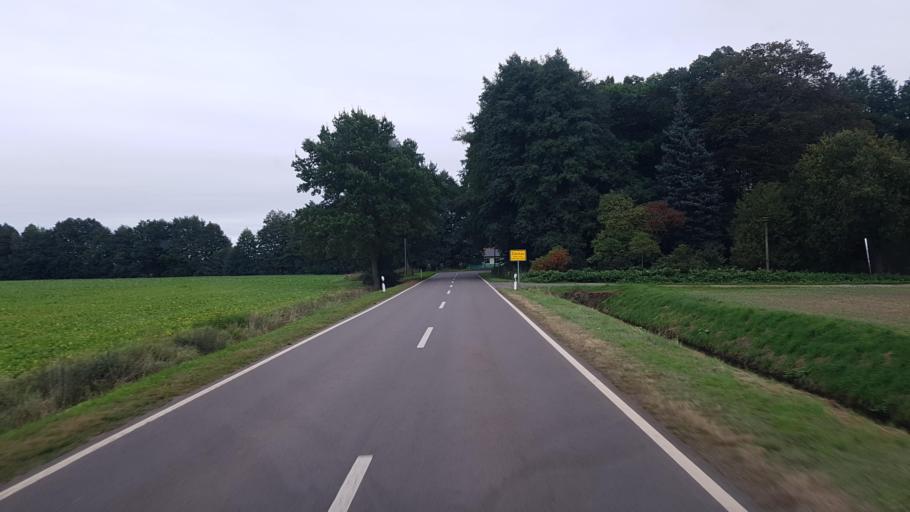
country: DE
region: Brandenburg
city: Drahnsdorf
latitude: 51.8952
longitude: 13.6411
